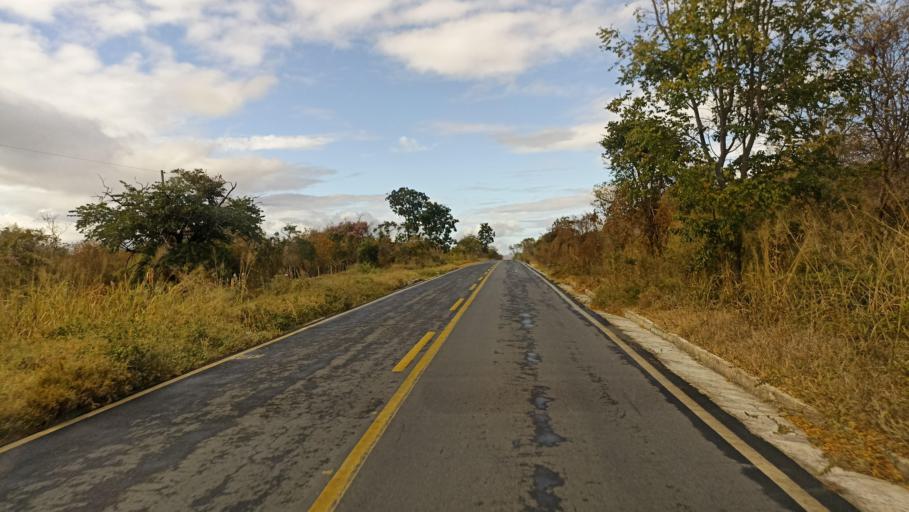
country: BR
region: Minas Gerais
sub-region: Itinga
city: Itinga
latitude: -16.5912
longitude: -41.6854
